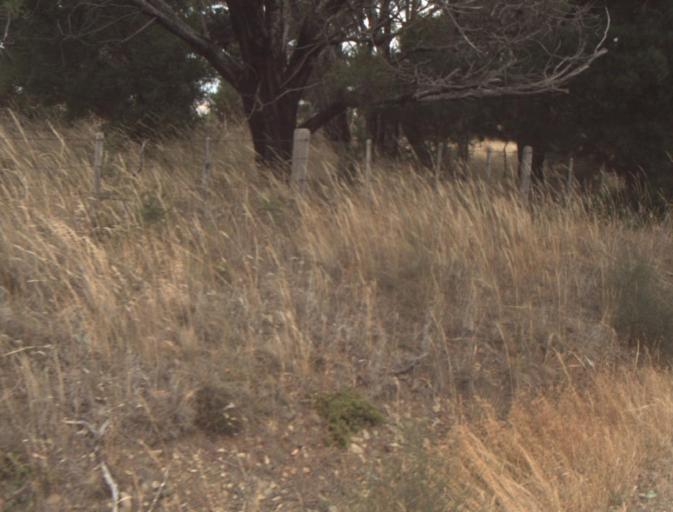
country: AU
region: Tasmania
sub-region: Northern Midlands
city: Evandale
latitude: -41.5134
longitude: 147.2982
